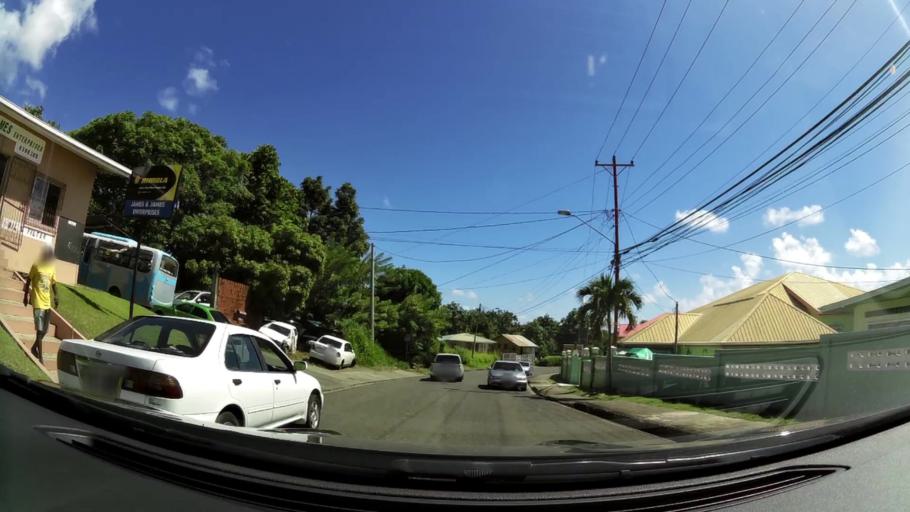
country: TT
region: Tobago
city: Scarborough
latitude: 11.1753
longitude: -60.7865
